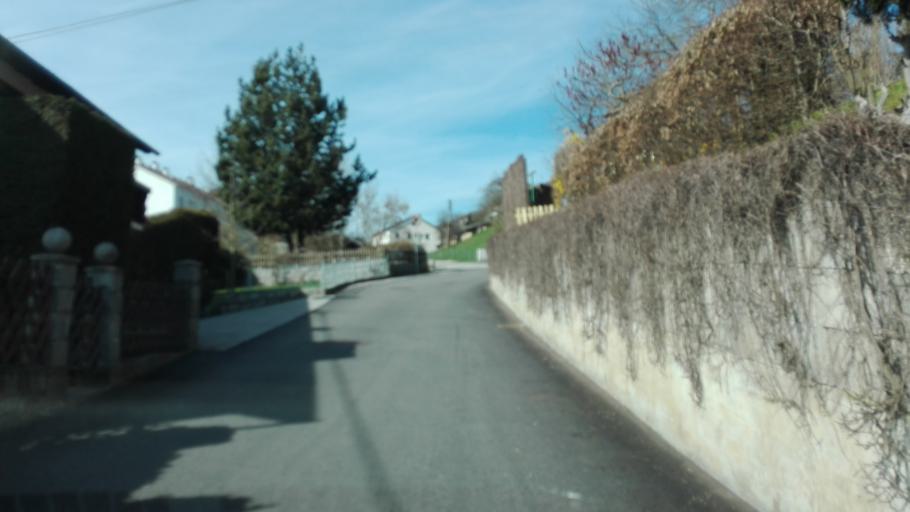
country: AT
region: Lower Austria
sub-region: Politischer Bezirk Amstetten
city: Ennsdorf
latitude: 48.2496
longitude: 14.5036
